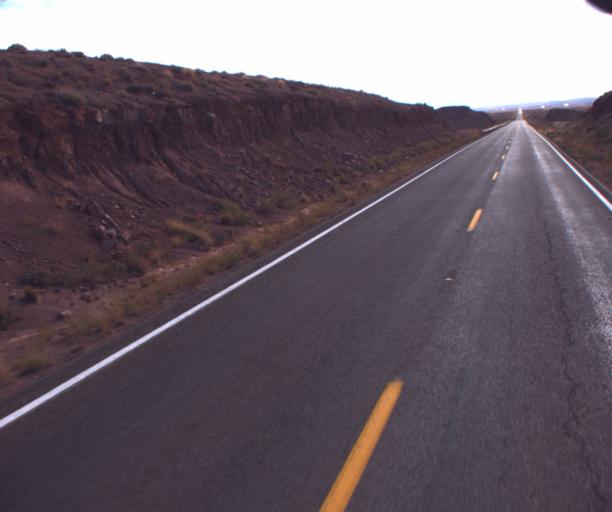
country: US
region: Arizona
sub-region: Apache County
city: Many Farms
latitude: 36.5398
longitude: -109.5216
